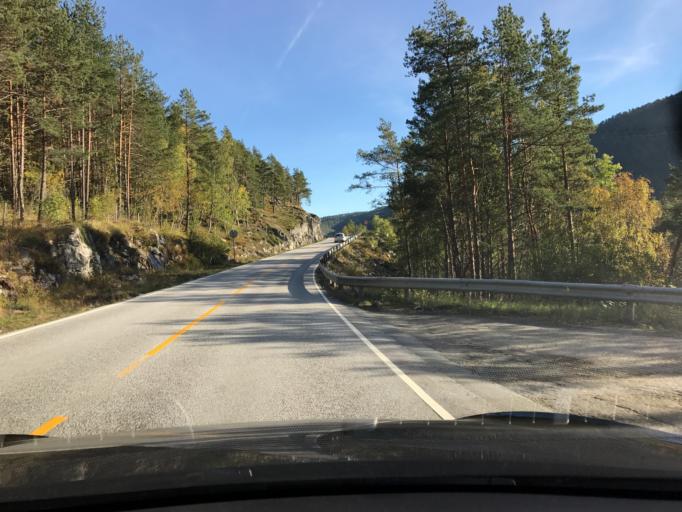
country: NO
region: Sogn og Fjordane
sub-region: Sogndal
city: Sogndalsfjora
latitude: 61.2095
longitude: 7.1553
